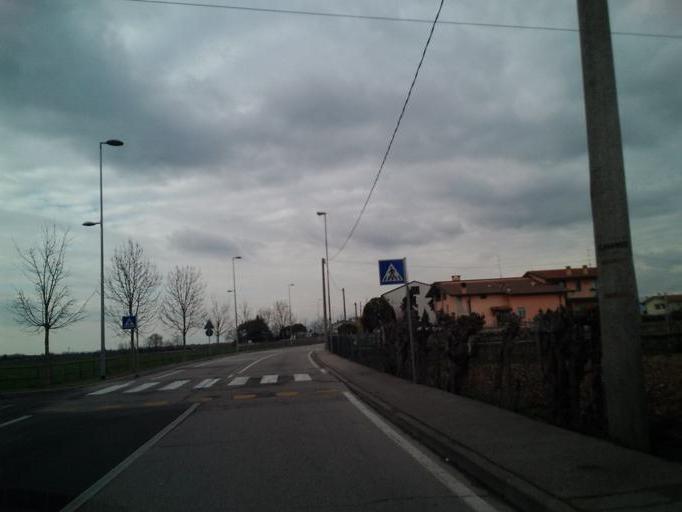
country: IT
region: Veneto
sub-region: Provincia di Verona
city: Alpo
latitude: 45.3785
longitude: 10.9199
